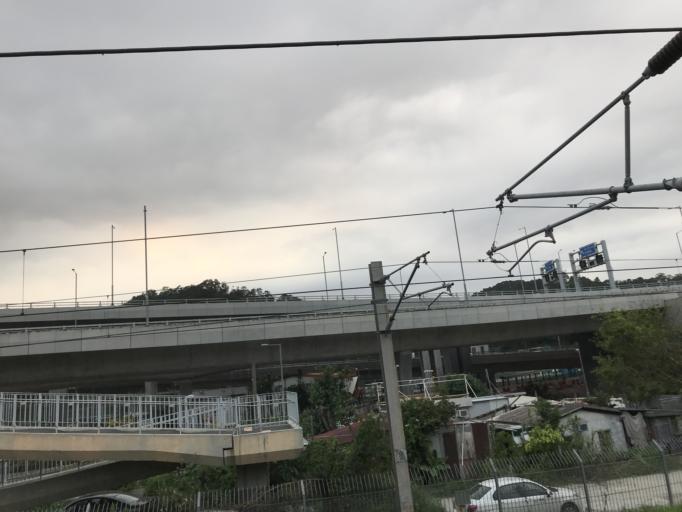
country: HK
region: Tai Po
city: Tai Po
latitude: 22.4807
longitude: 114.1553
